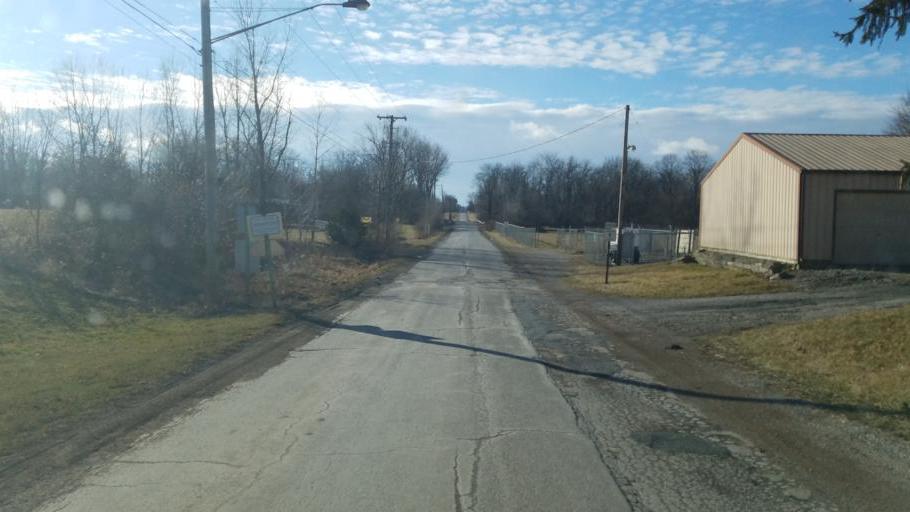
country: US
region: Ohio
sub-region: Morrow County
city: Mount Gilead
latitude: 40.5539
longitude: -82.8628
